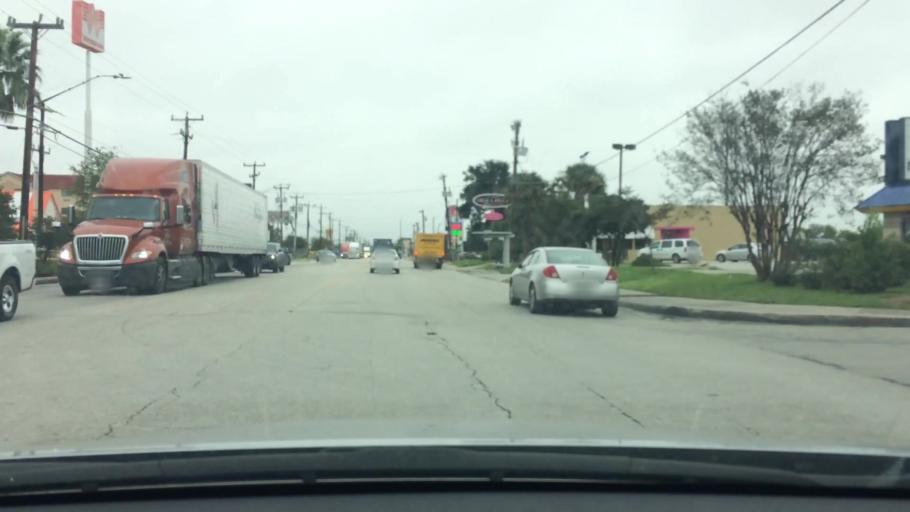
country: US
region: Texas
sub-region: Bexar County
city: Kirby
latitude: 29.4840
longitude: -98.4016
